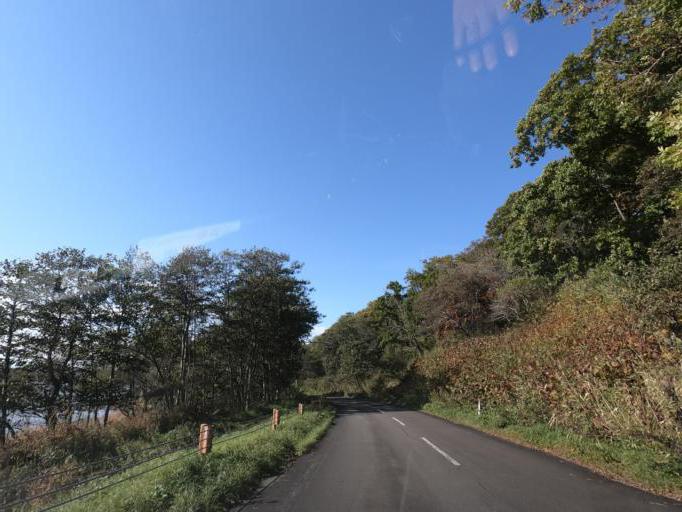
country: JP
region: Hokkaido
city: Obihiro
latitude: 42.6072
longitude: 143.5501
